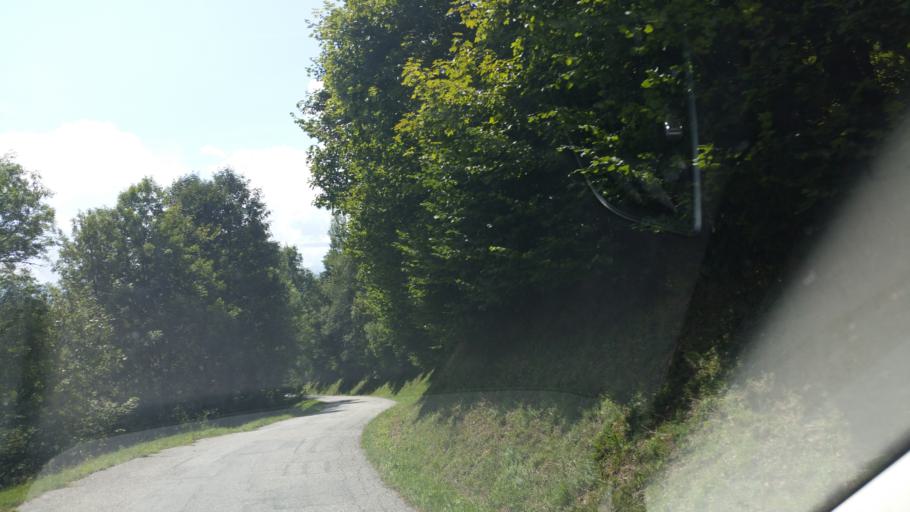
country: FR
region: Rhone-Alpes
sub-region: Departement de la Savoie
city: La Chambre
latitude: 45.4094
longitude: 6.3350
